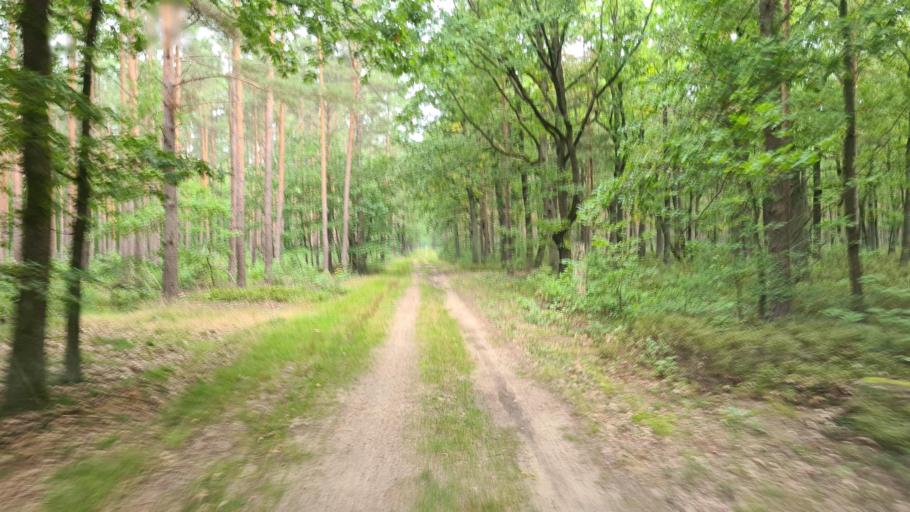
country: DE
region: Brandenburg
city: Hohenbucko
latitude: 51.7772
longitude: 13.5498
